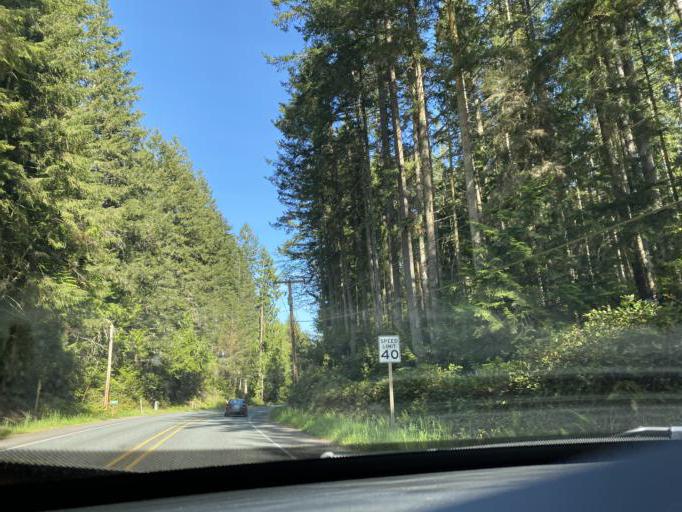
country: US
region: Washington
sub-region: Island County
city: Langley
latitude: 48.0330
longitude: -122.4402
